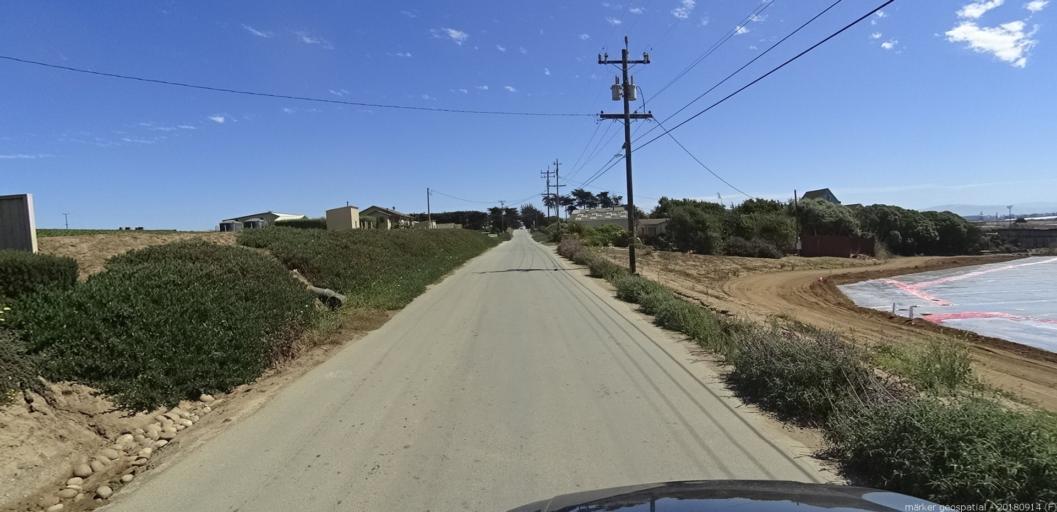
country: US
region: California
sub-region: Monterey County
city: Las Lomas
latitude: 36.8557
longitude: -121.7944
